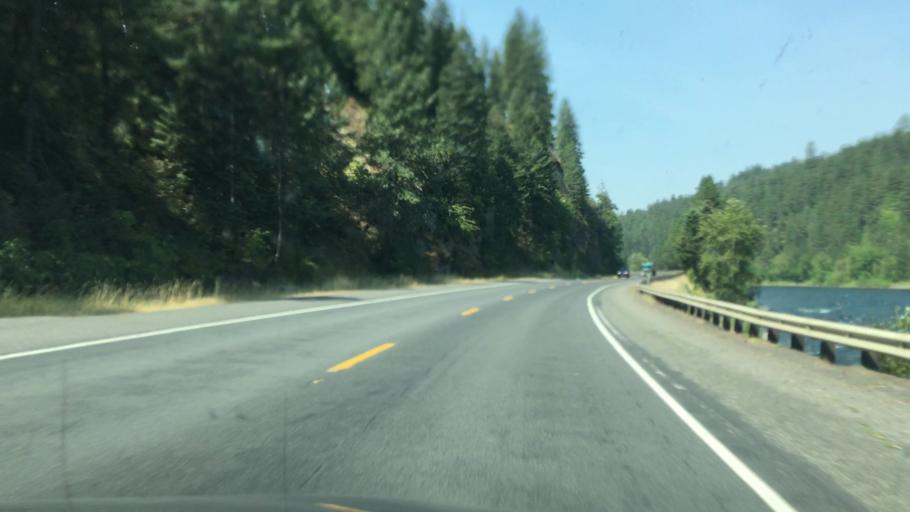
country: US
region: Idaho
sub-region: Clearwater County
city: Orofino
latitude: 46.5017
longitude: -116.3559
